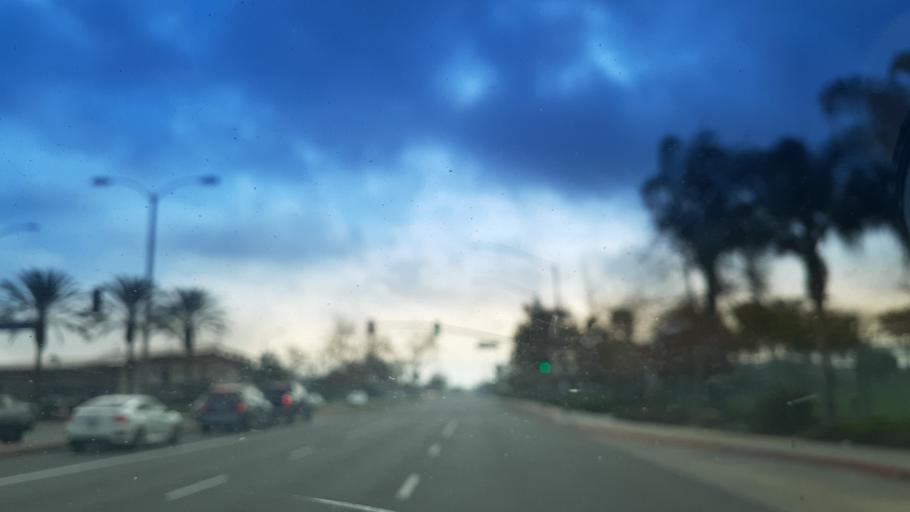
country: US
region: California
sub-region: Orange County
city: Costa Mesa
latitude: 33.6595
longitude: -117.9193
